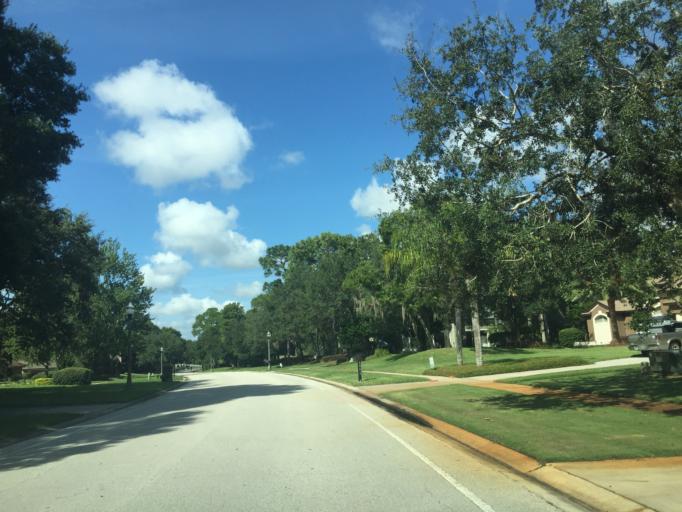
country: US
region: Florida
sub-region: Seminole County
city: Oviedo
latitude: 28.6676
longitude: -81.2394
